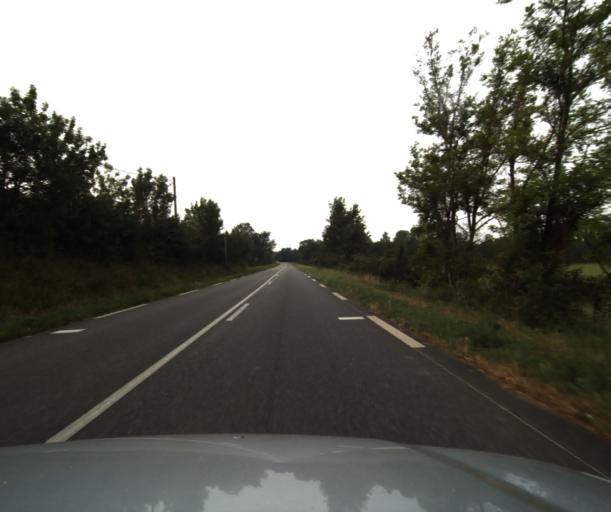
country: FR
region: Midi-Pyrenees
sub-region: Departement du Gers
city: Gimont
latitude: 43.7062
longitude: 0.8519
